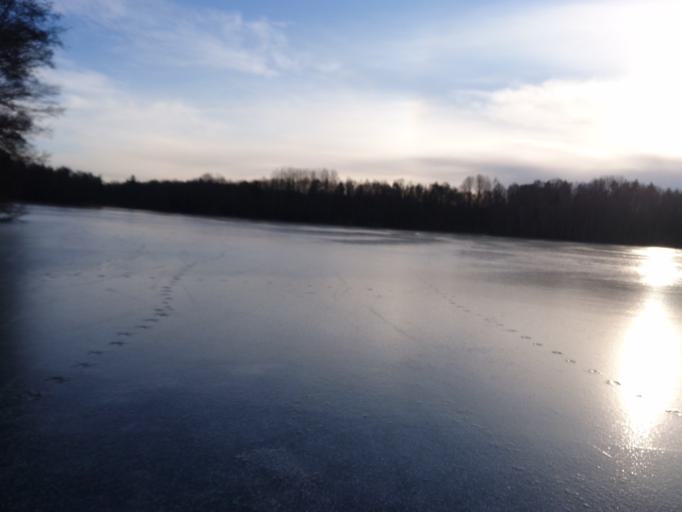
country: SE
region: Blekinge
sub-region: Karlshamns Kommun
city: Karlshamn
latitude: 56.2370
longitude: 14.9688
